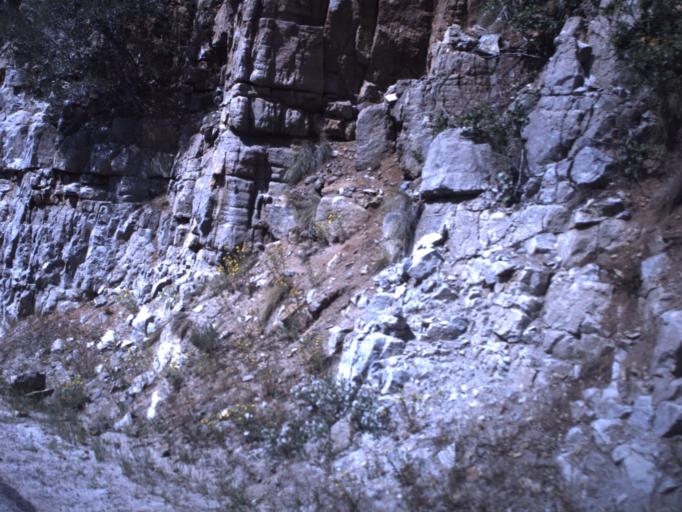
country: US
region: Idaho
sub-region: Bear Lake County
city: Paris
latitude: 41.9591
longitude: -111.5161
